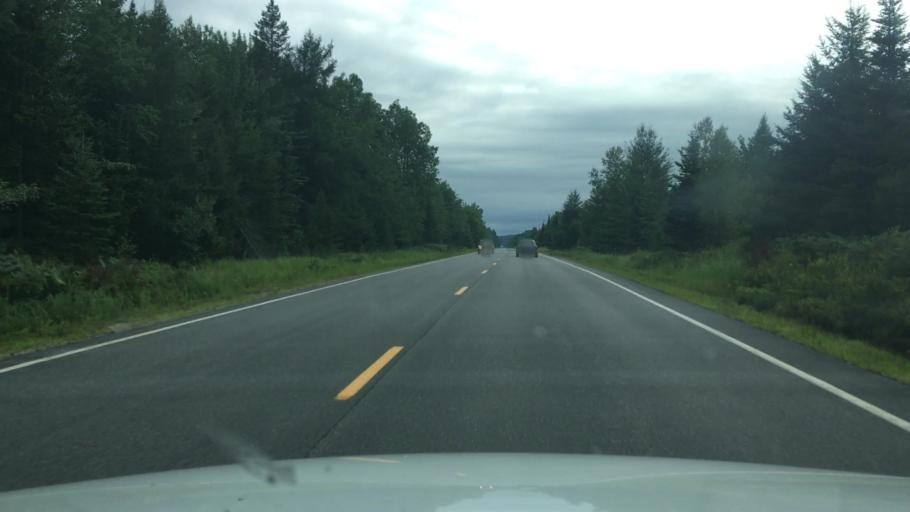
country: US
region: Maine
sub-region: Washington County
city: Cherryfield
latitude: 44.6067
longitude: -67.8932
